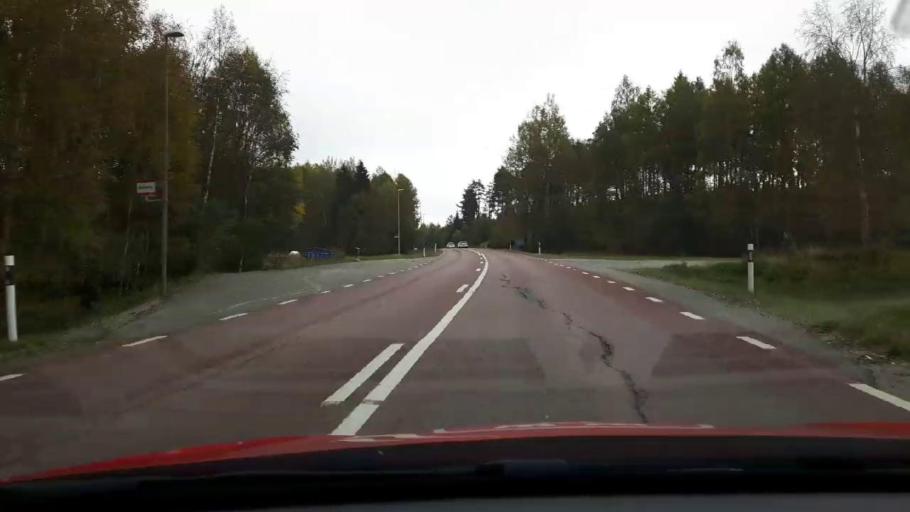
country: SE
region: Gaevleborg
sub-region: Ljusdals Kommun
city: Farila
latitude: 61.8005
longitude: 15.7991
